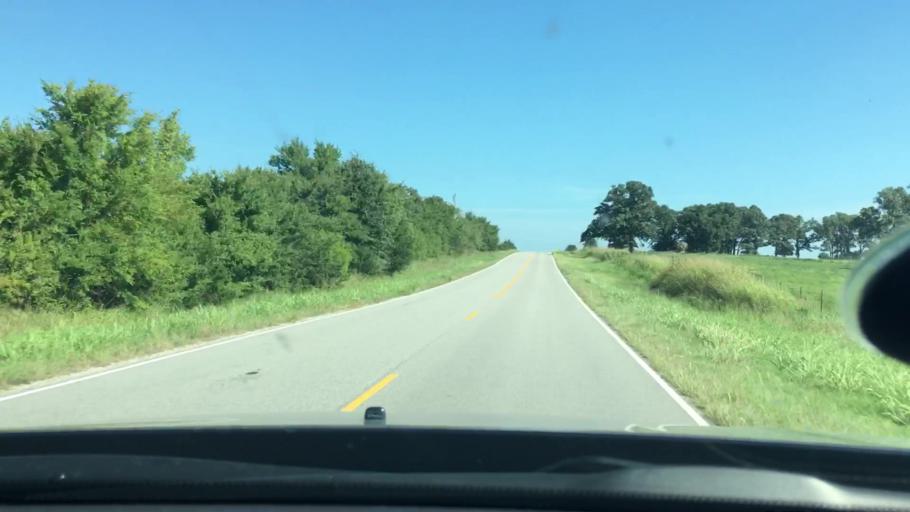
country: US
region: Oklahoma
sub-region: Johnston County
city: Tishomingo
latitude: 34.3491
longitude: -96.5488
